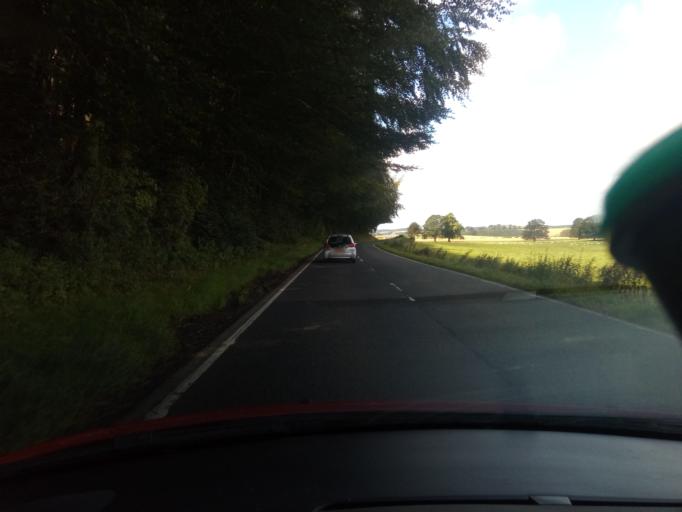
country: GB
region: Scotland
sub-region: The Scottish Borders
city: Jedburgh
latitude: 55.5729
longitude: -2.5461
